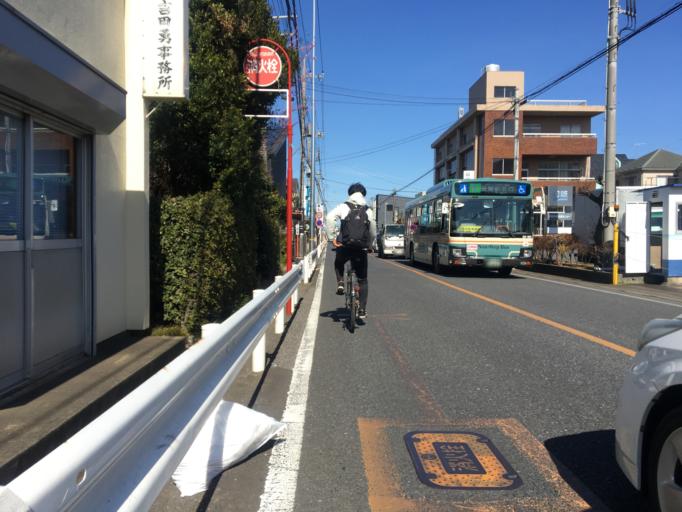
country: JP
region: Saitama
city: Shiki
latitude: 35.8088
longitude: 139.5645
